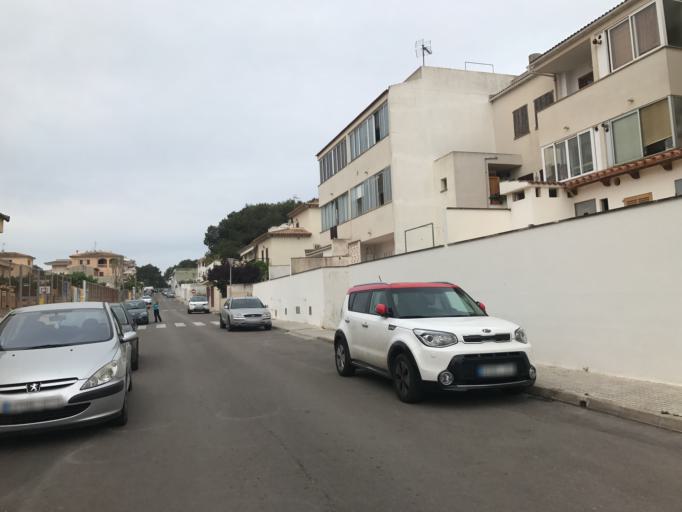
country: ES
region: Balearic Islands
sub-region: Illes Balears
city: Santa Margalida
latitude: 39.7632
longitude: 3.1543
